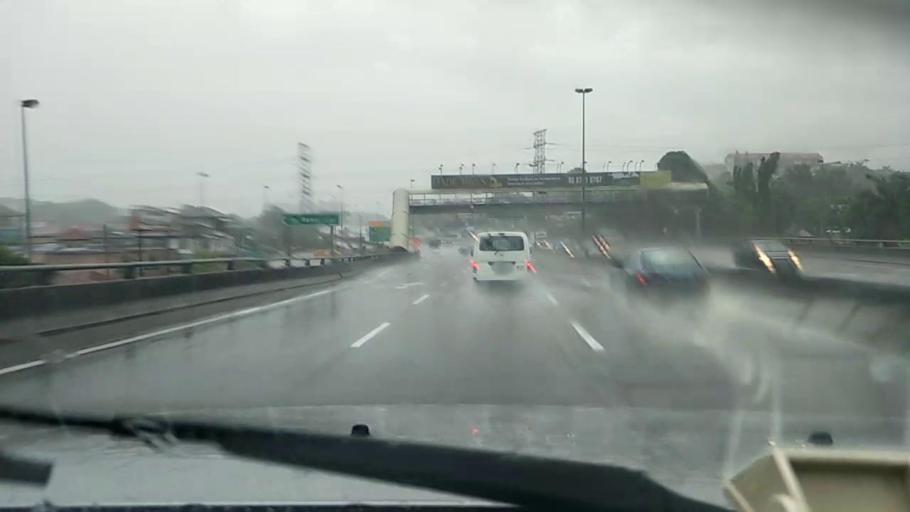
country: MY
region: Selangor
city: Kampong Baharu Balakong
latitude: 2.9866
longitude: 101.7667
